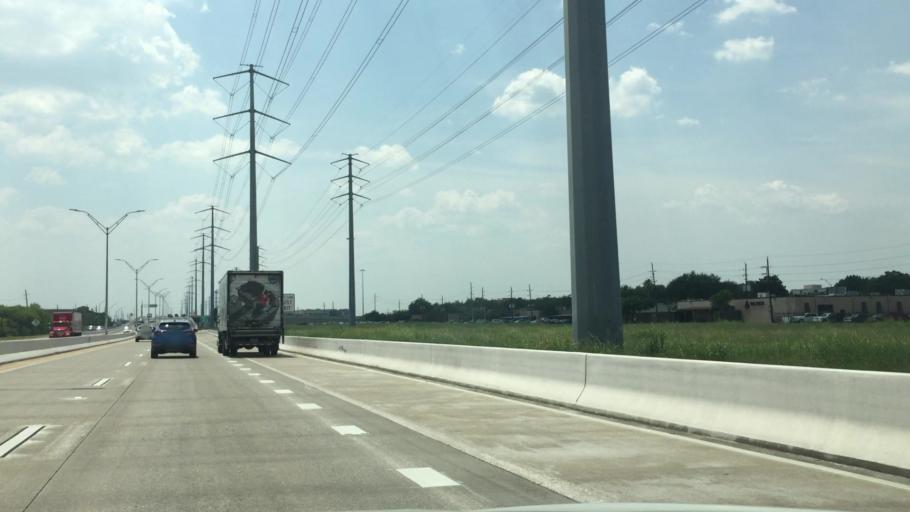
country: US
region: Texas
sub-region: Harris County
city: Bunker Hill Village
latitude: 29.7196
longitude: -95.5496
